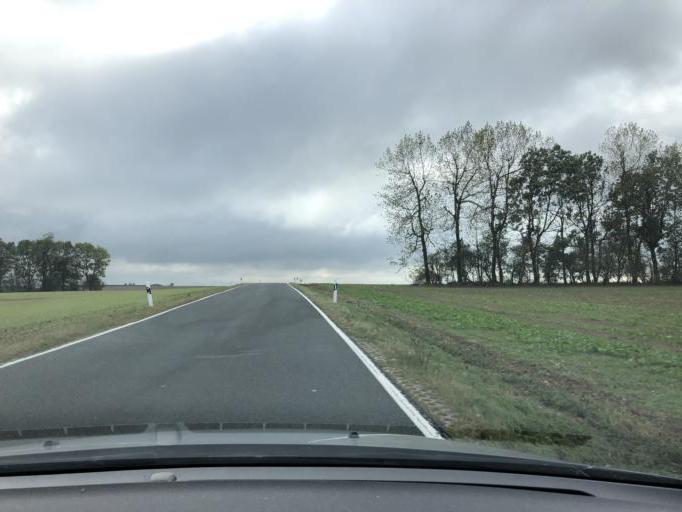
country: DE
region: Thuringia
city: Wachstedt
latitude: 51.3081
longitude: 10.2356
